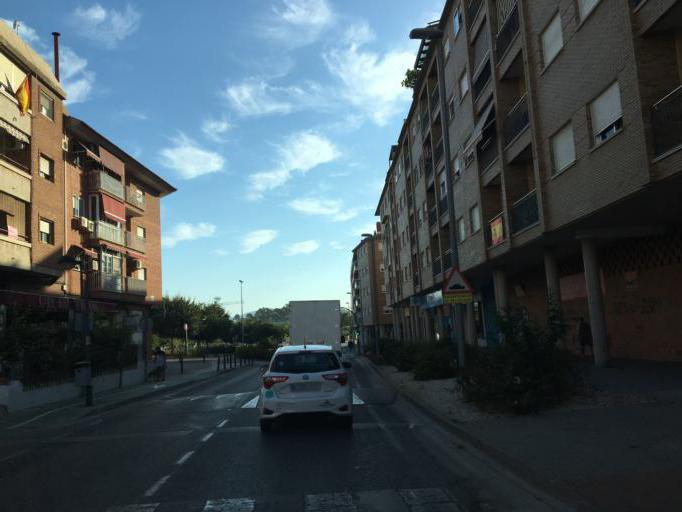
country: ES
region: Murcia
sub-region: Murcia
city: Murcia
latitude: 38.0286
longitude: -1.1250
